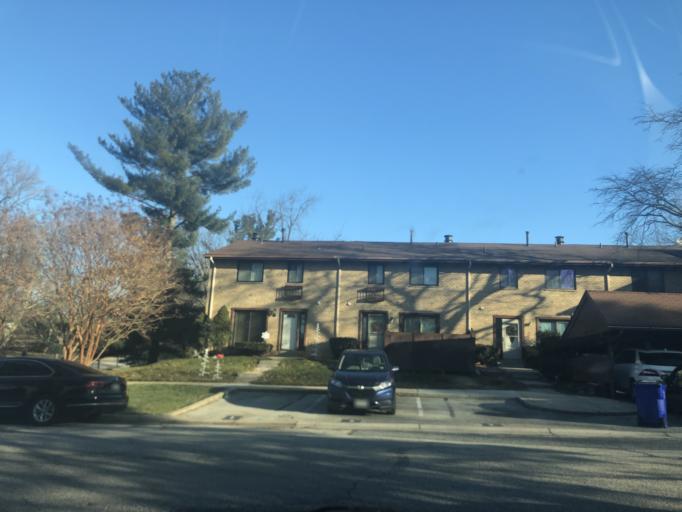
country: US
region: Maryland
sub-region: Howard County
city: Columbia
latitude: 39.2074
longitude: -76.8300
